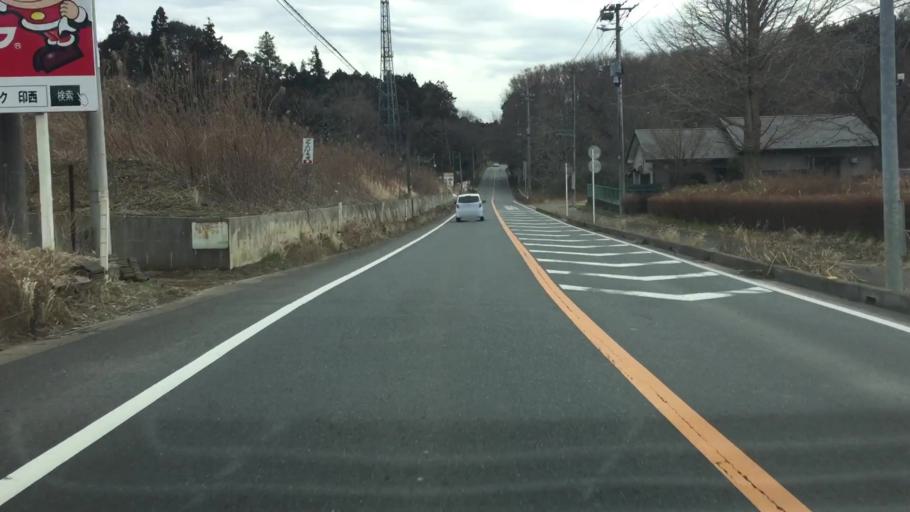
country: JP
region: Ibaraki
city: Ryugasaki
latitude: 35.8233
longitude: 140.1695
